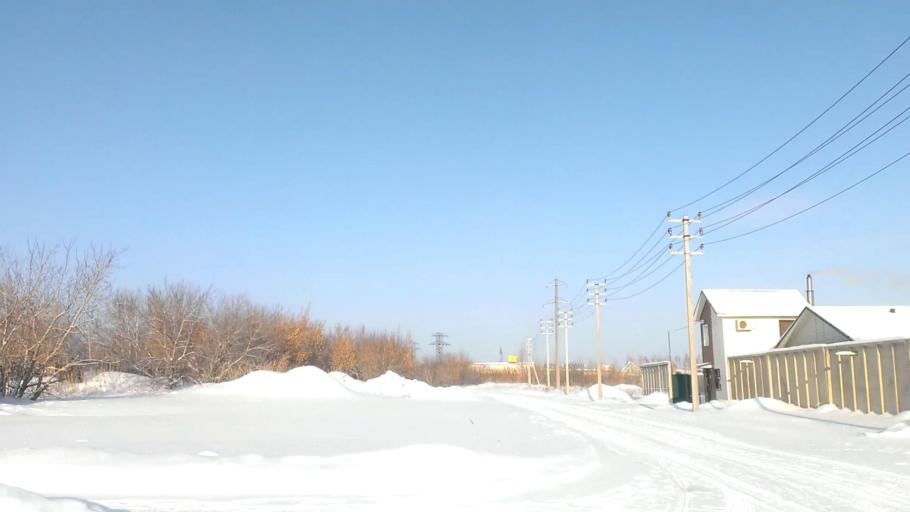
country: RU
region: Altai Krai
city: Novosilikatnyy
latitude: 53.3438
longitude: 83.6298
